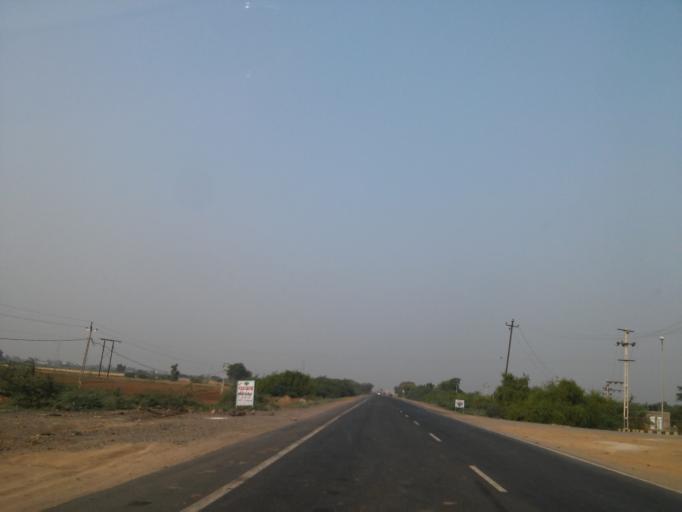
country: IN
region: Gujarat
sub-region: Kachchh
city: Anjar
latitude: 23.2936
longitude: 70.0822
